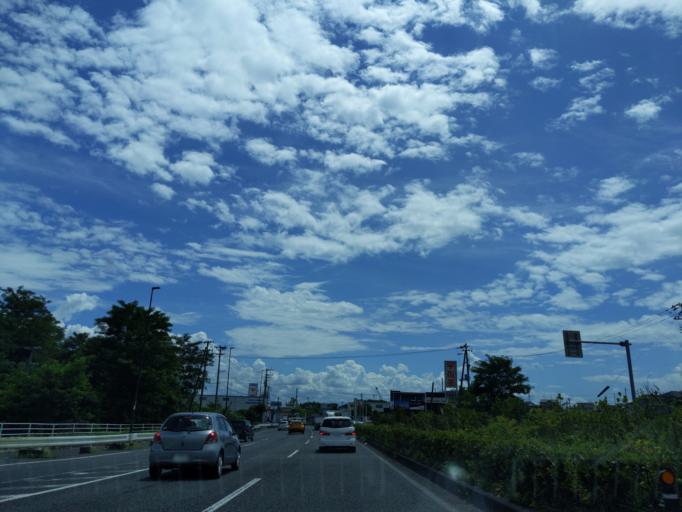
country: JP
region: Fukushima
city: Sukagawa
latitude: 37.3364
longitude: 140.3611
